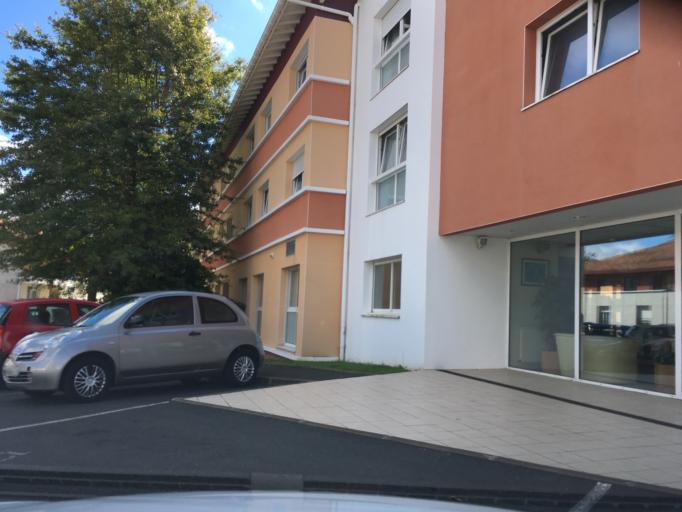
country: FR
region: Aquitaine
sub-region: Departement des Pyrenees-Atlantiques
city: Boucau
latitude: 43.5026
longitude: -1.4611
